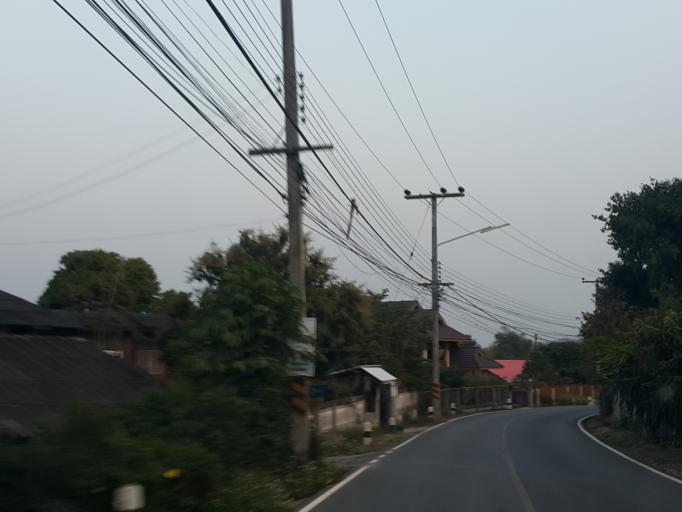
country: TH
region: Chiang Mai
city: Mae Taeng
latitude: 19.0222
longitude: 98.8753
